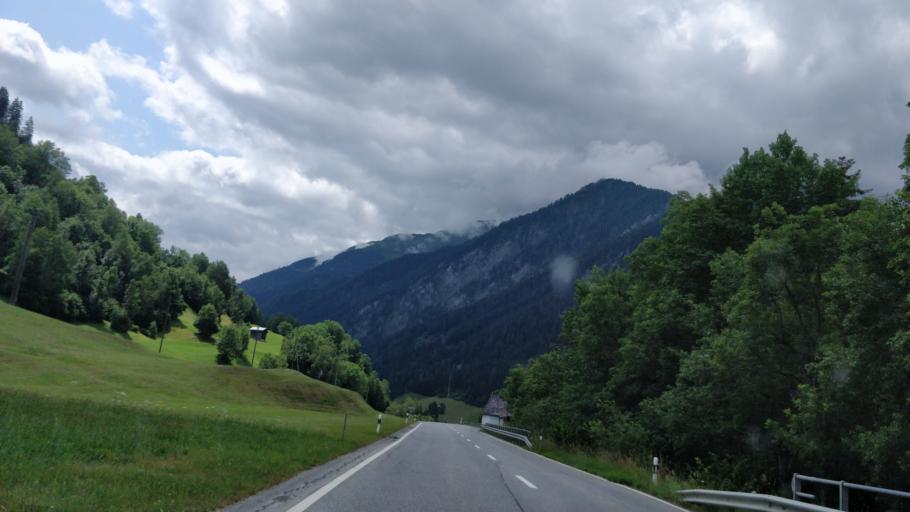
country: CH
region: Grisons
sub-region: Surselva District
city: Ilanz
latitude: 46.6916
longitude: 9.1817
